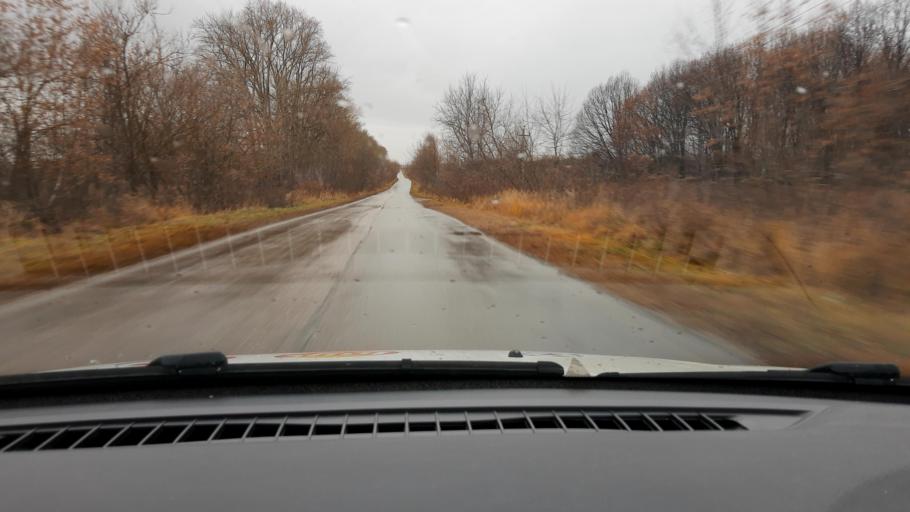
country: RU
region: Nizjnij Novgorod
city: Dzerzhinsk
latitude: 56.1777
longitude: 43.4934
